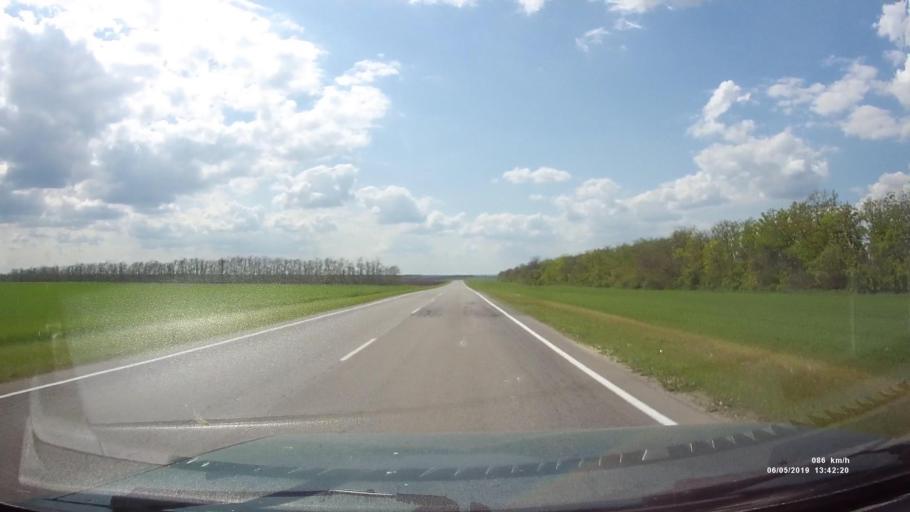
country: RU
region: Rostov
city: Semikarakorsk
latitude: 47.6605
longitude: 40.6593
